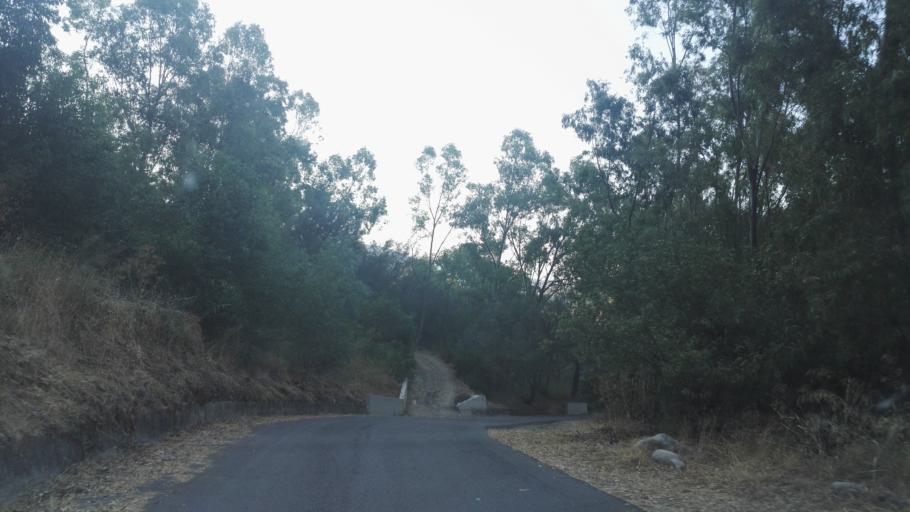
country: IT
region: Calabria
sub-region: Provincia di Reggio Calabria
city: Placanica
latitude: 38.4198
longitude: 16.4469
